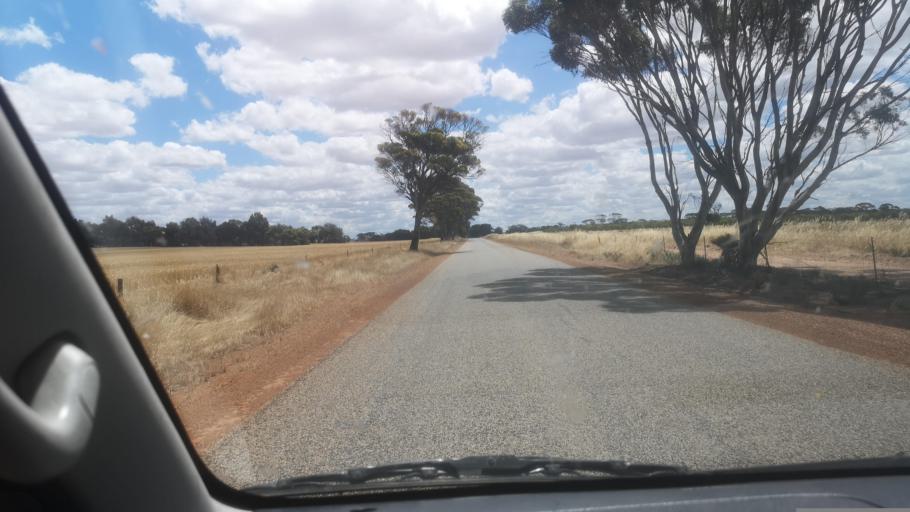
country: AU
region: Western Australia
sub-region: Cunderdin
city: Cunderdin
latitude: -32.0777
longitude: 117.4730
